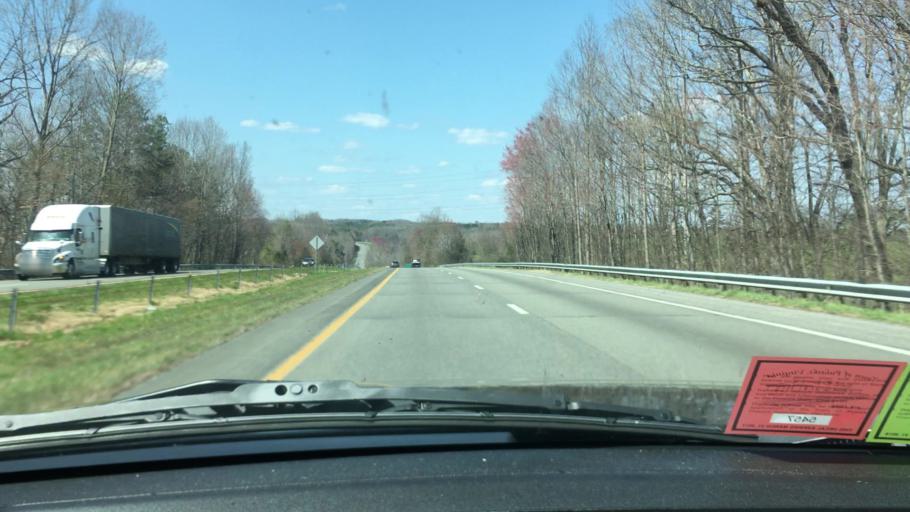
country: US
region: North Carolina
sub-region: Surry County
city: Pilot Mountain
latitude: 36.3902
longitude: -80.4901
